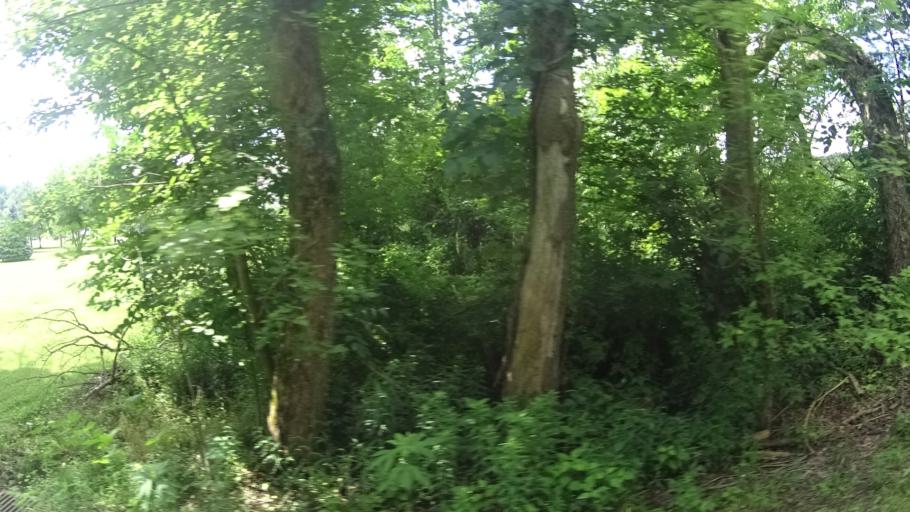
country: US
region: Ohio
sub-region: Huron County
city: Wakeman
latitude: 41.2944
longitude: -82.3802
